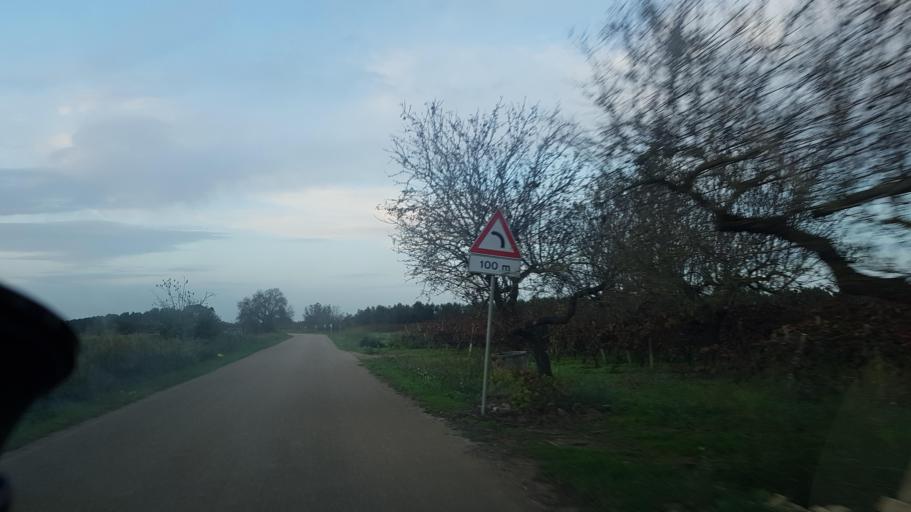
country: IT
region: Apulia
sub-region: Provincia di Brindisi
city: San Donaci
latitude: 40.4293
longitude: 17.9315
